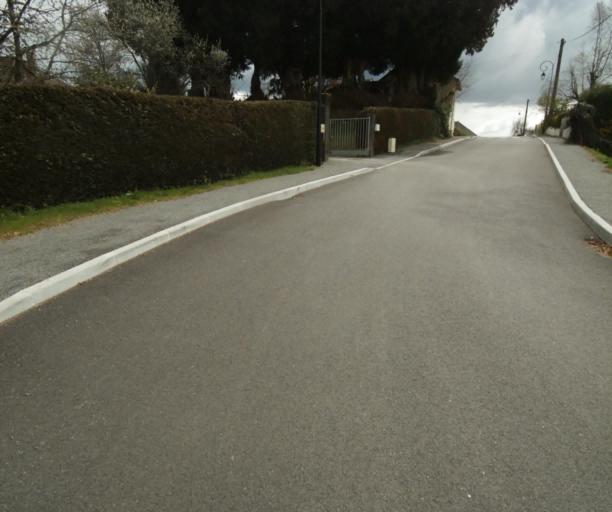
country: FR
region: Limousin
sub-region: Departement de la Correze
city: Correze
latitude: 45.2796
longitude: 1.9731
